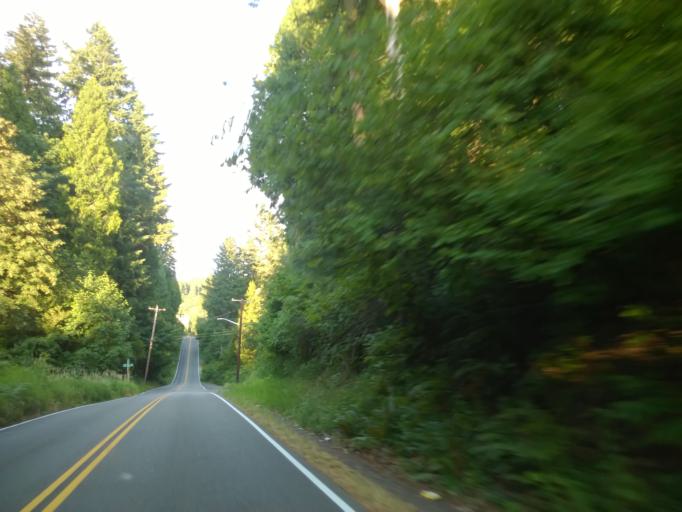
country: US
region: Washington
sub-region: King County
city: Woodinville
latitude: 47.7763
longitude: -122.1582
